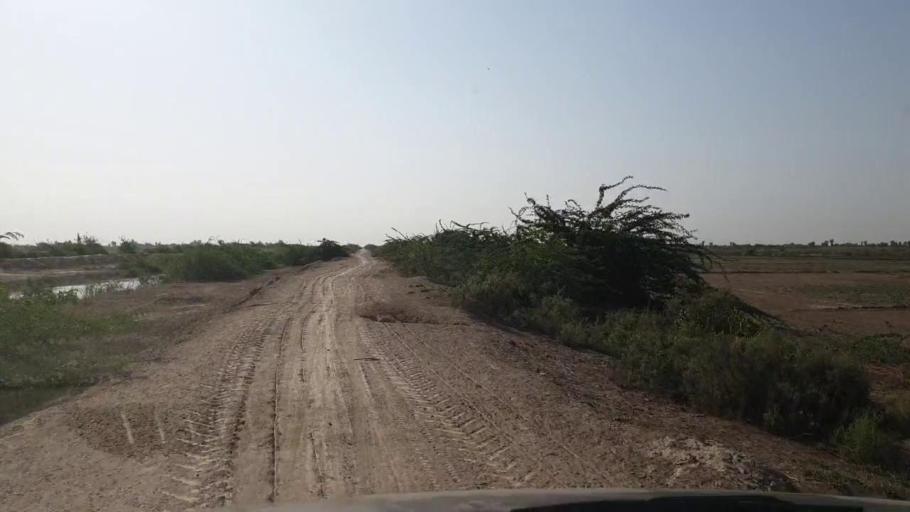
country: PK
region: Sindh
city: Kadhan
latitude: 24.5825
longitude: 69.0791
